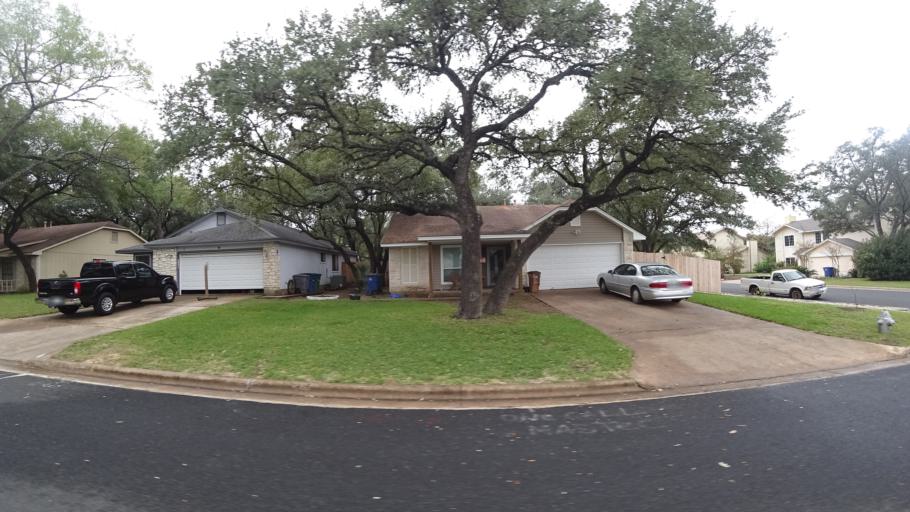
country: US
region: Texas
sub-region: Travis County
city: Shady Hollow
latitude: 30.2072
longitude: -97.8441
